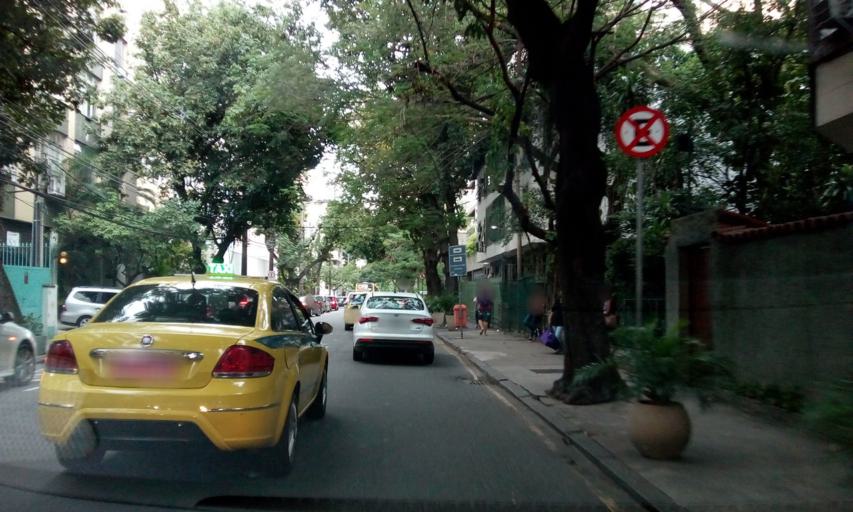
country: BR
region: Rio de Janeiro
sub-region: Rio De Janeiro
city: Rio de Janeiro
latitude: -22.9762
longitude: -43.2281
